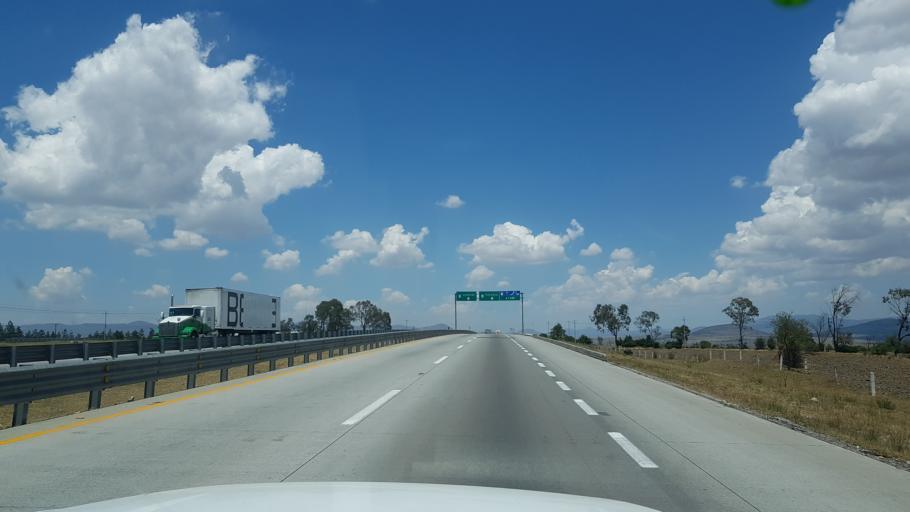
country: MX
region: Tlaxcala
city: Sanctorum
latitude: 19.5407
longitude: -98.4877
